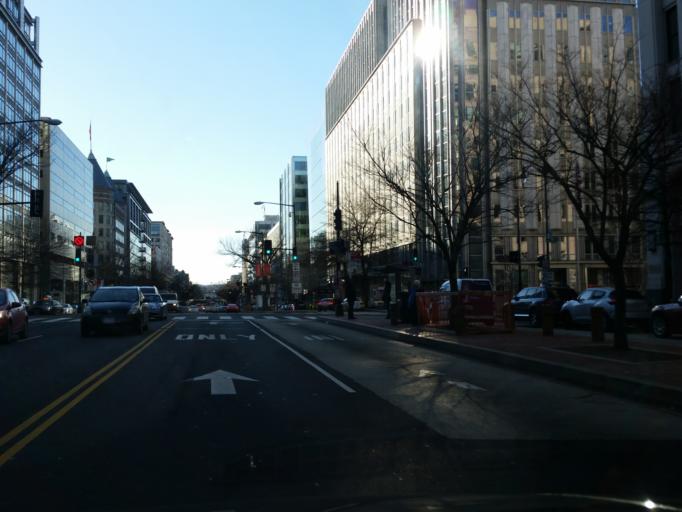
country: US
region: Washington, D.C.
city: Washington, D.C.
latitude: 38.9025
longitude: -77.0429
